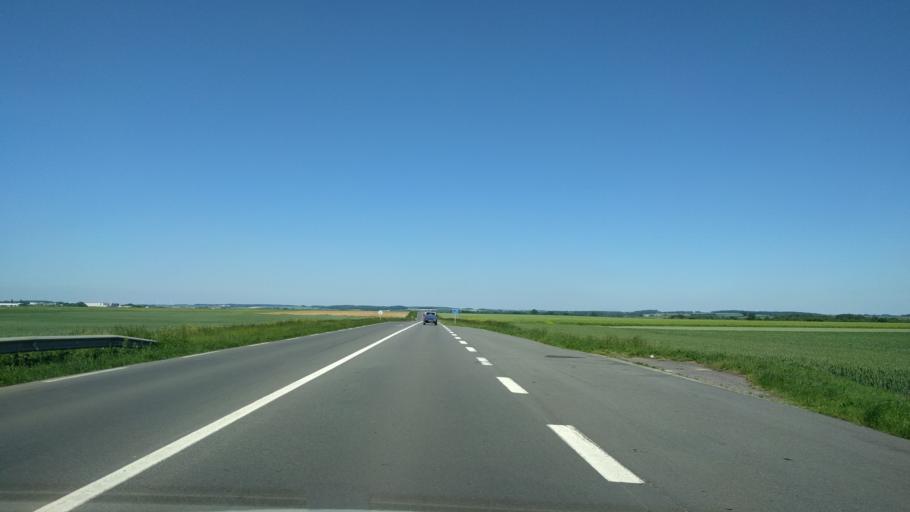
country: FR
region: Picardie
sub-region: Departement de la Somme
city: Peronne
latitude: 49.8801
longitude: 2.8986
